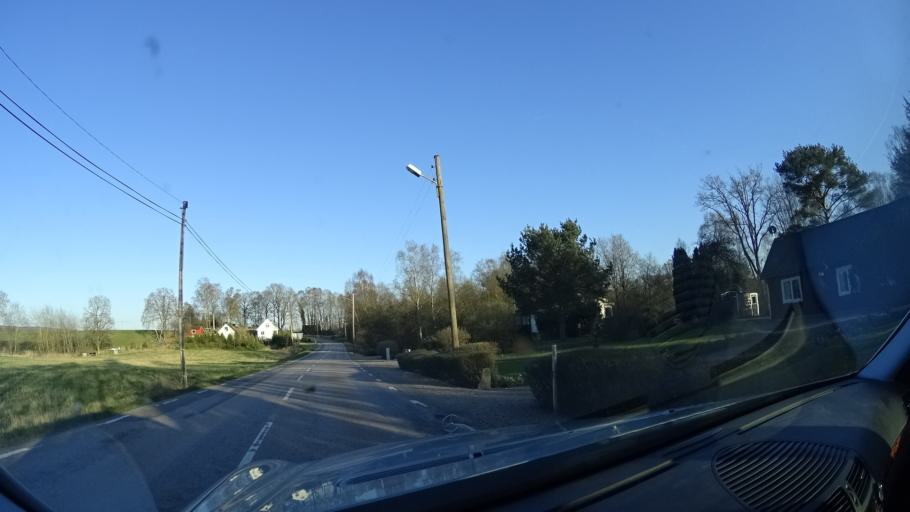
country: SE
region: Skane
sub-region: Bjuvs Kommun
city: Billesholm
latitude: 56.0456
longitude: 13.0050
